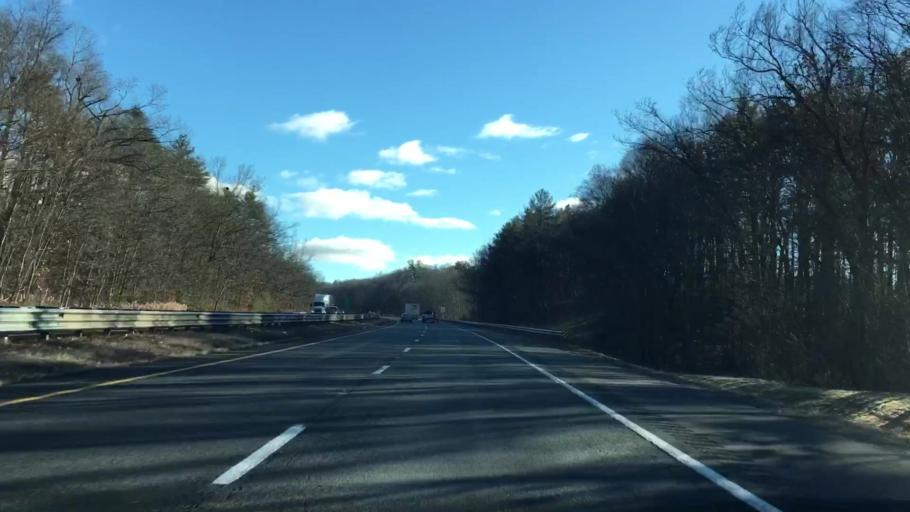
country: US
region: Massachusetts
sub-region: Worcester County
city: Fiskdale
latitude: 42.1341
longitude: -72.1218
